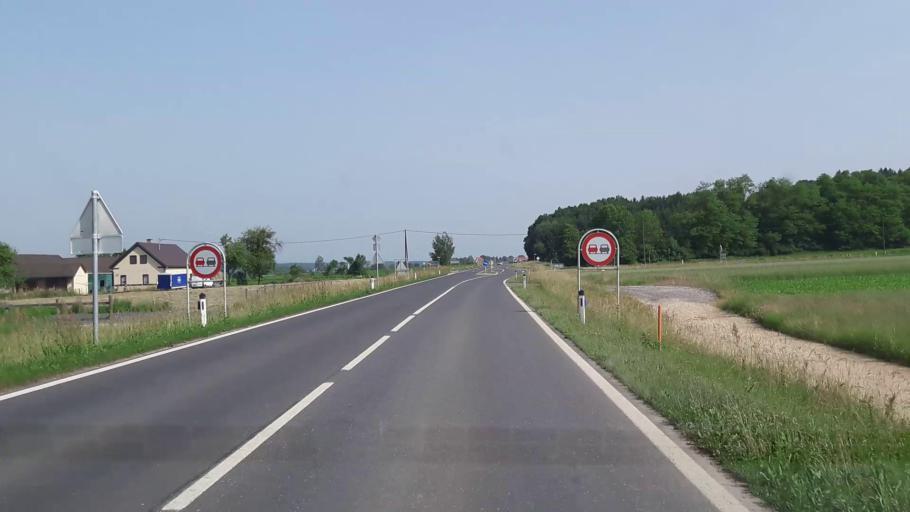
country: AT
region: Burgenland
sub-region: Politischer Bezirk Jennersdorf
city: Rudersdorf
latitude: 47.0664
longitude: 16.1142
